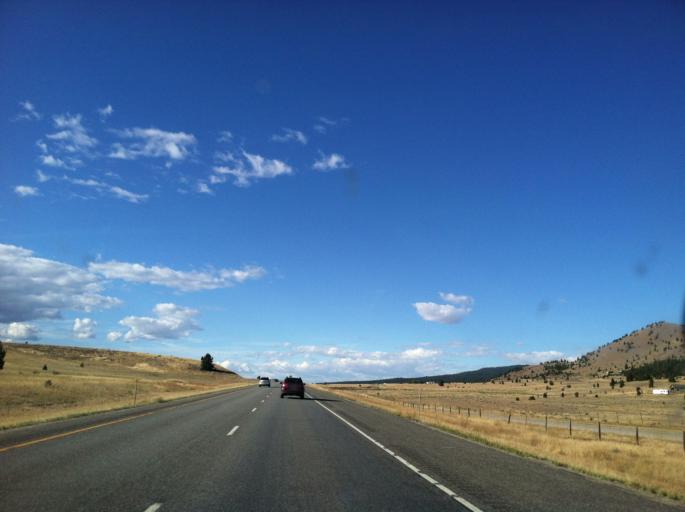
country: US
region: Montana
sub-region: Silver Bow County
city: Butte-Silver Bow (Balance)
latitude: 46.0345
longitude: -112.7325
